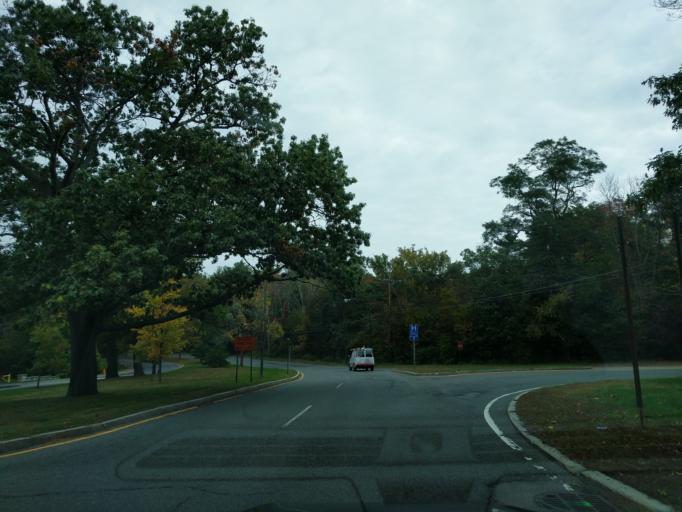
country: US
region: Massachusetts
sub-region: Middlesex County
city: Melrose
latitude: 42.4551
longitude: -71.0900
